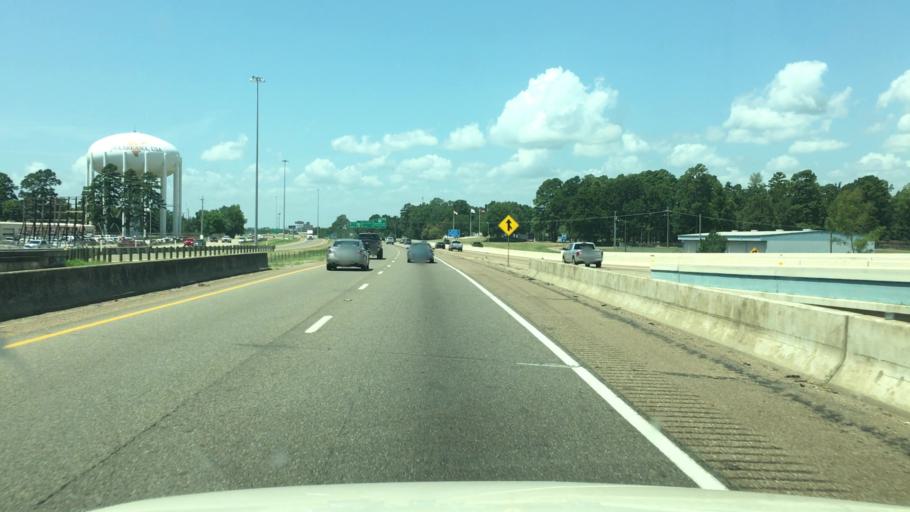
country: US
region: Arkansas
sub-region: Miller County
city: Texarkana
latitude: 33.4703
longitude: -94.0505
